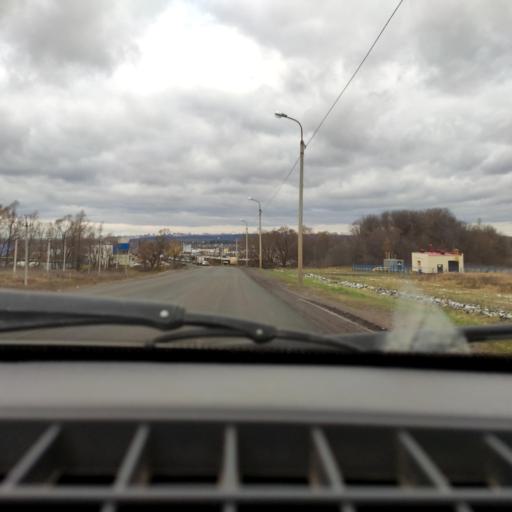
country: RU
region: Bashkortostan
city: Kabakovo
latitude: 54.6391
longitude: 56.0915
